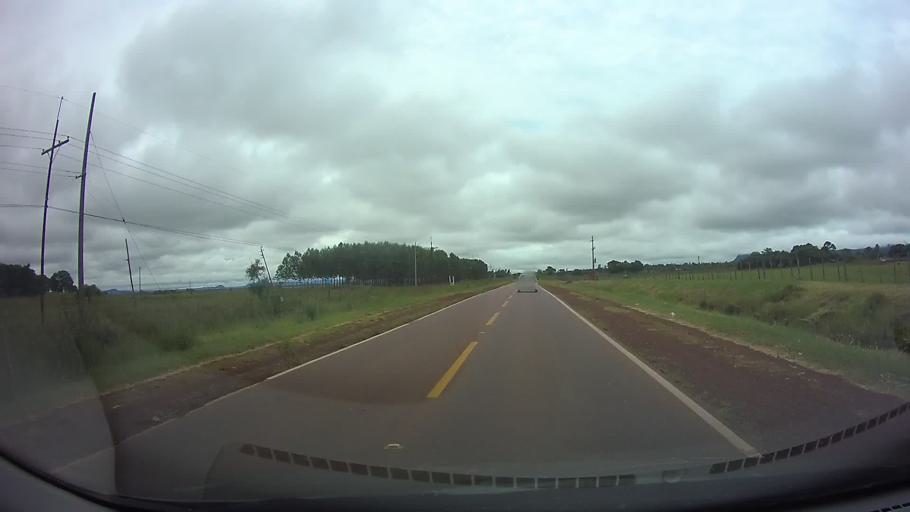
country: PY
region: Paraguari
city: Carapegua
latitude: -25.8048
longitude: -57.1870
